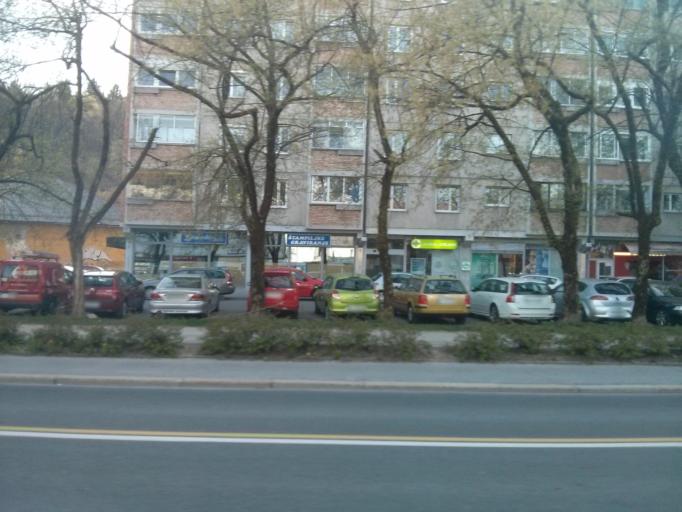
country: SI
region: Ljubljana
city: Ljubljana
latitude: 46.0651
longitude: 14.4936
